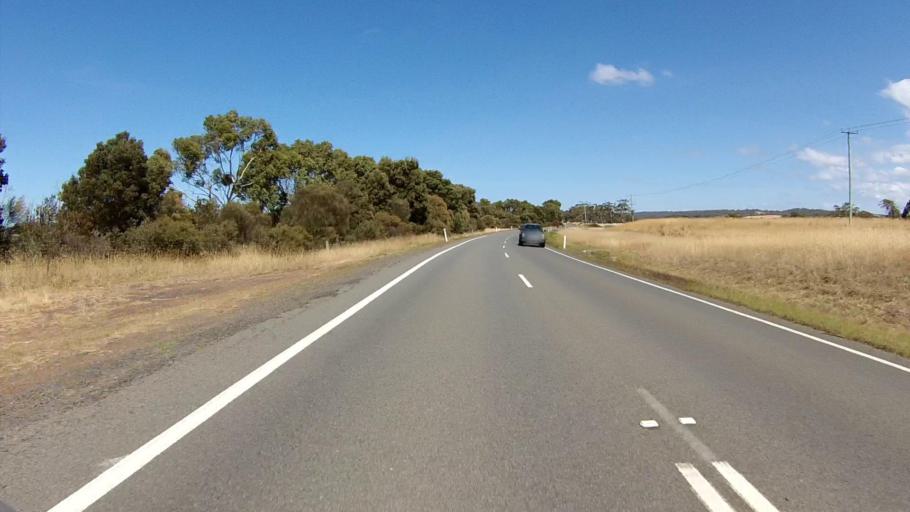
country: AU
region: Tasmania
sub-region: Break O'Day
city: St Helens
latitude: -42.1072
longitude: 148.0566
